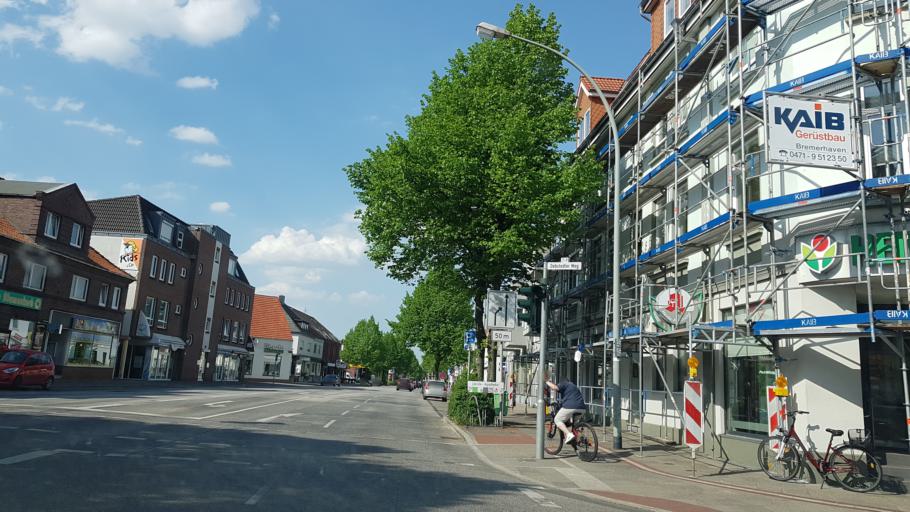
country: DE
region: Lower Saxony
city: Langen
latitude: 53.5898
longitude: 8.5974
